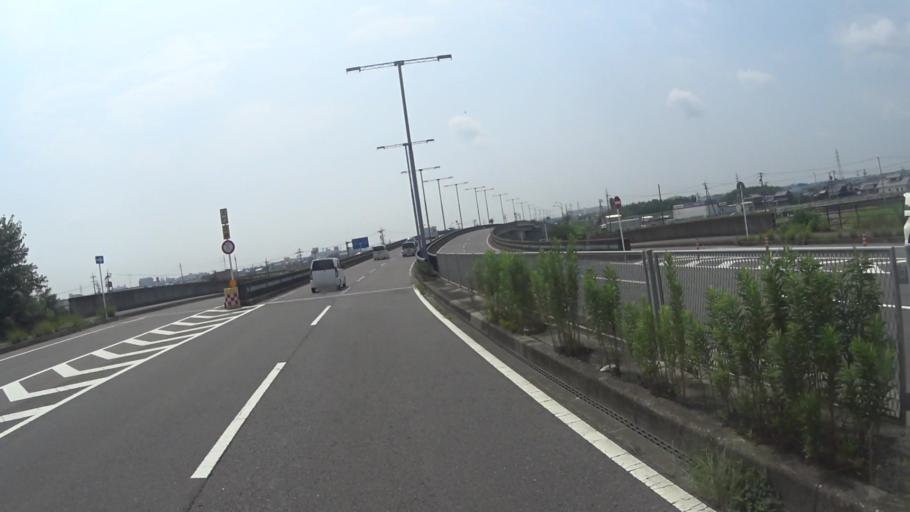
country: JP
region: Mie
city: Suzuka
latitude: 34.8805
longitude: 136.5191
